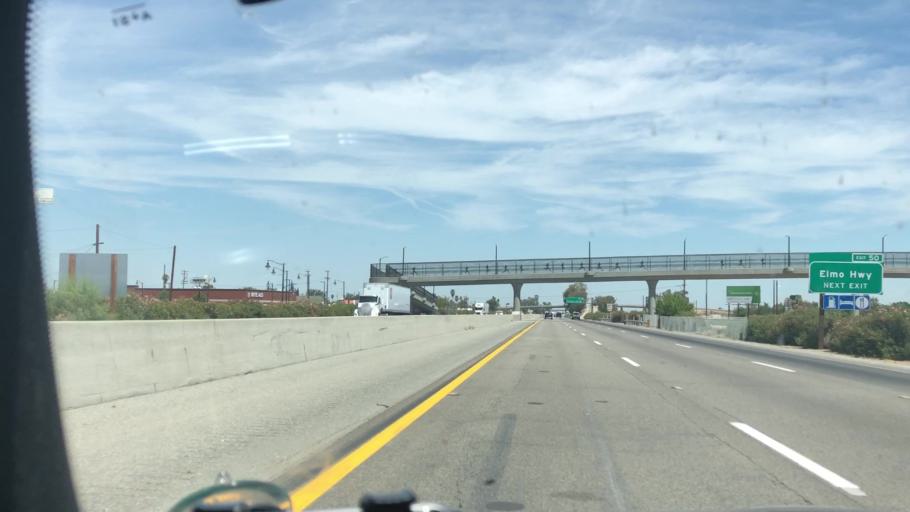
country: US
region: California
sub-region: Kern County
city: McFarland
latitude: 35.6767
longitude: -119.2271
